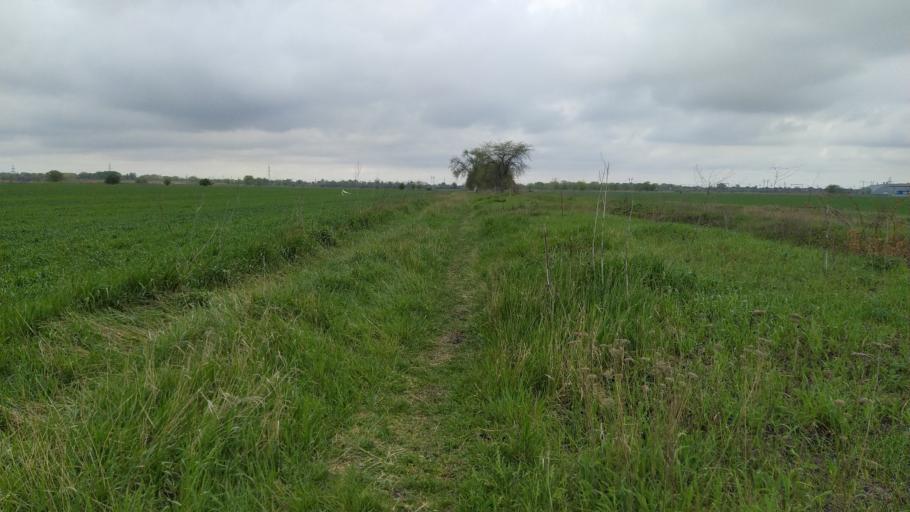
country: RU
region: Rostov
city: Bataysk
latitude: 47.1238
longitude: 39.7279
